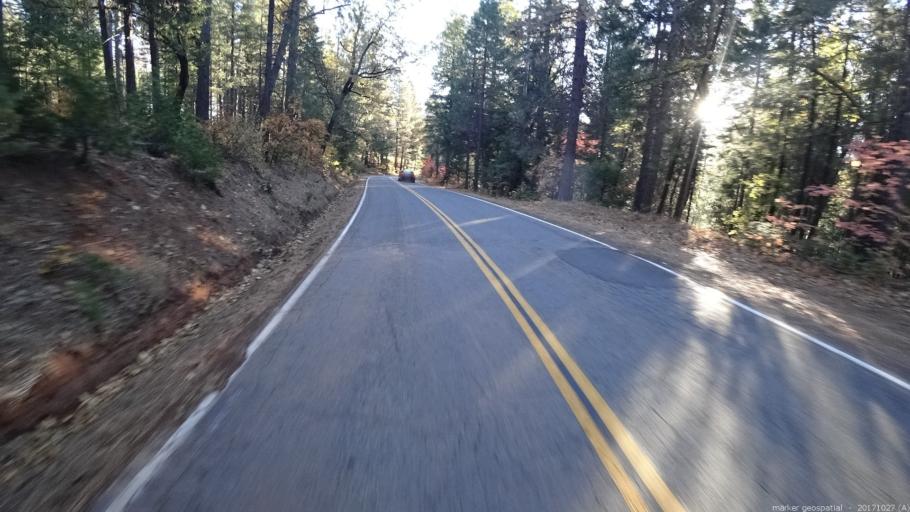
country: US
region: California
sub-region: Shasta County
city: Burney
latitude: 40.9248
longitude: -121.9199
